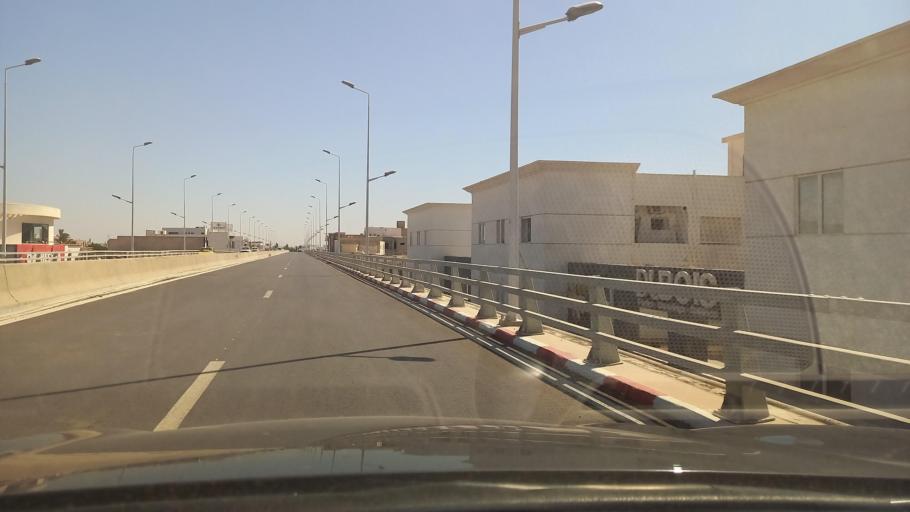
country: TN
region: Safaqis
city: Sfax
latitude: 34.7633
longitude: 10.7419
